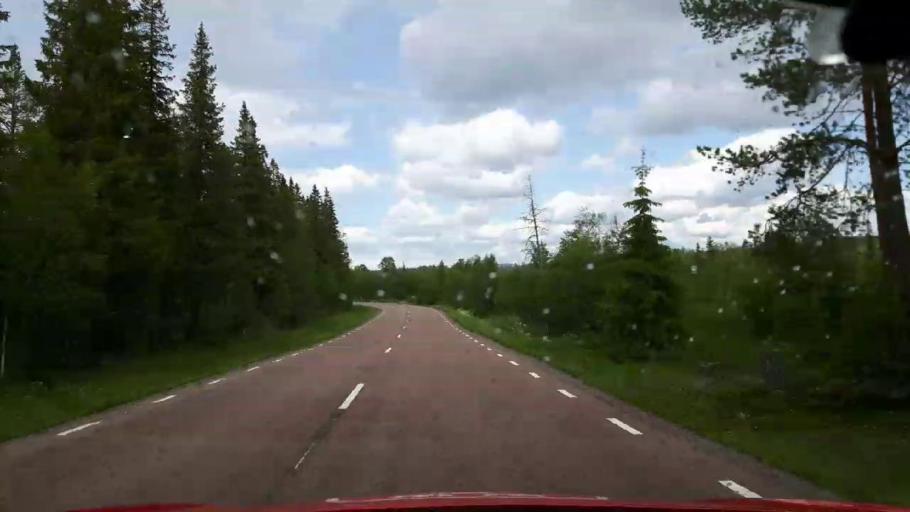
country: SE
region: Jaemtland
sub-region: Krokoms Kommun
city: Valla
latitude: 63.9441
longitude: 14.2259
